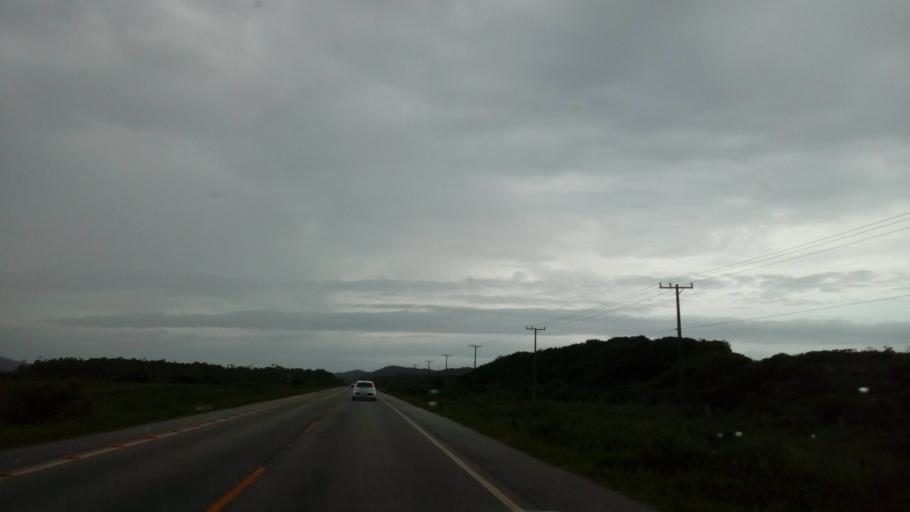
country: BR
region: Santa Catarina
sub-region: Laguna
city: Laguna
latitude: -28.5443
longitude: -48.7917
